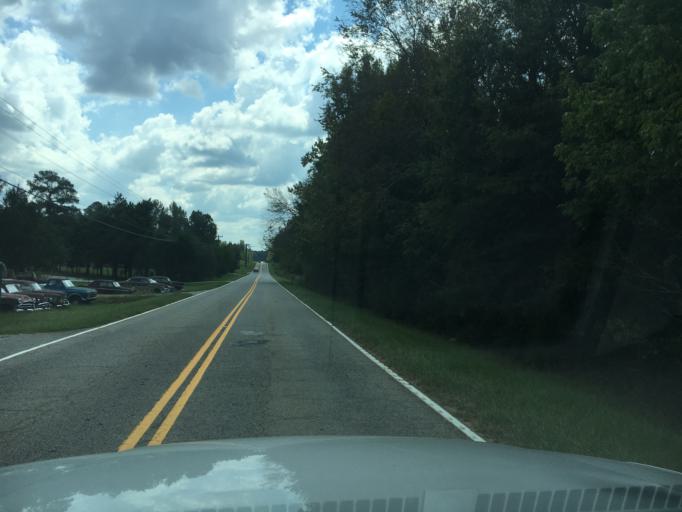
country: US
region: South Carolina
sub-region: Greenwood County
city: Greenwood
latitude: 34.1288
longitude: -82.1263
